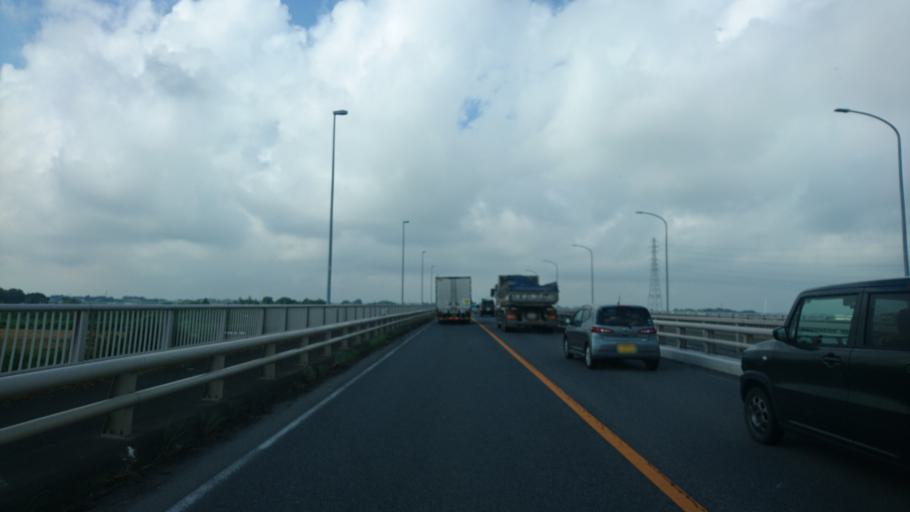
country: JP
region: Gunma
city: Tatebayashi
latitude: 36.2904
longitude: 139.5261
